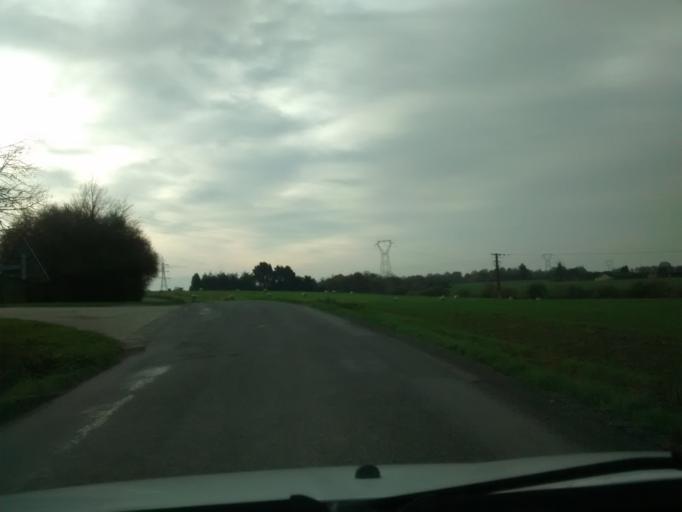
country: FR
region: Brittany
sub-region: Departement d'Ille-et-Vilaine
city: Noyal-sur-Vilaine
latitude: 48.0929
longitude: -1.5596
